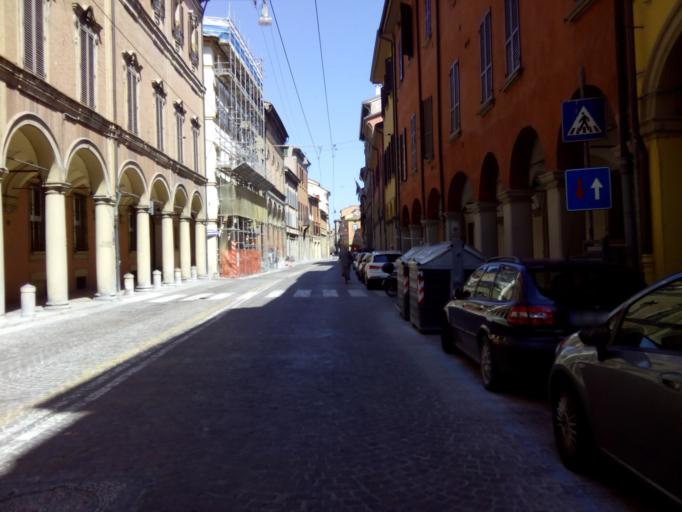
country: IT
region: Emilia-Romagna
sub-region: Provincia di Bologna
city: Bologna
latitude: 44.4882
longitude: 11.3520
